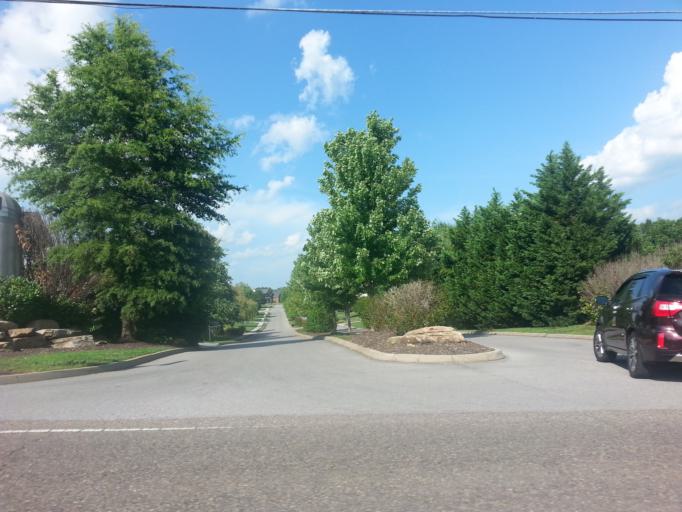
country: US
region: Tennessee
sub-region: Knox County
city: Knoxville
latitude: 36.0612
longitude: -83.8833
